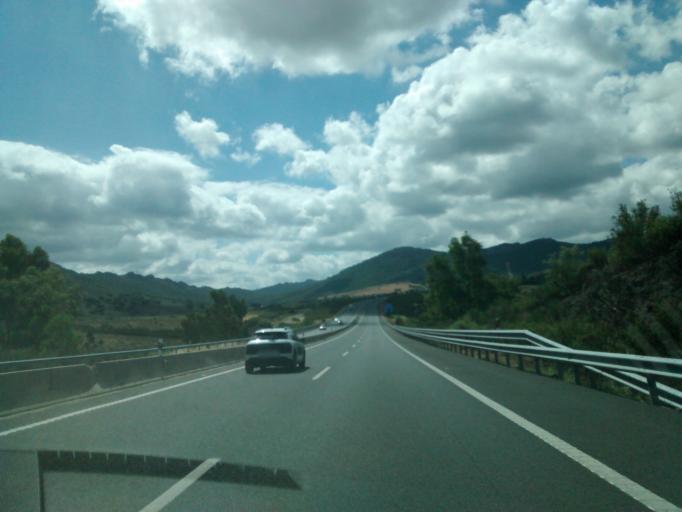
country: ES
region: Extremadura
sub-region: Provincia de Caceres
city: Romangordo
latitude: 39.7124
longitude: -5.6971
